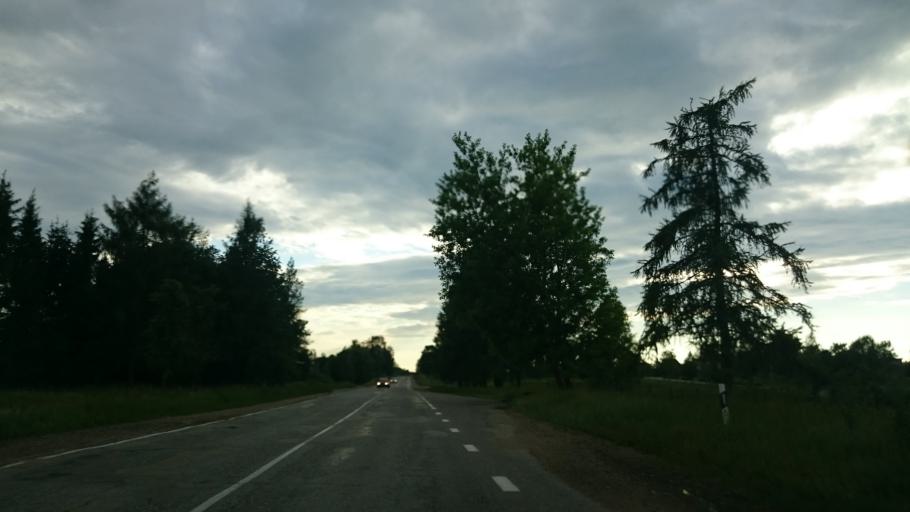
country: LV
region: Ludzas Rajons
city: Ludza
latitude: 56.5377
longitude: 27.6356
